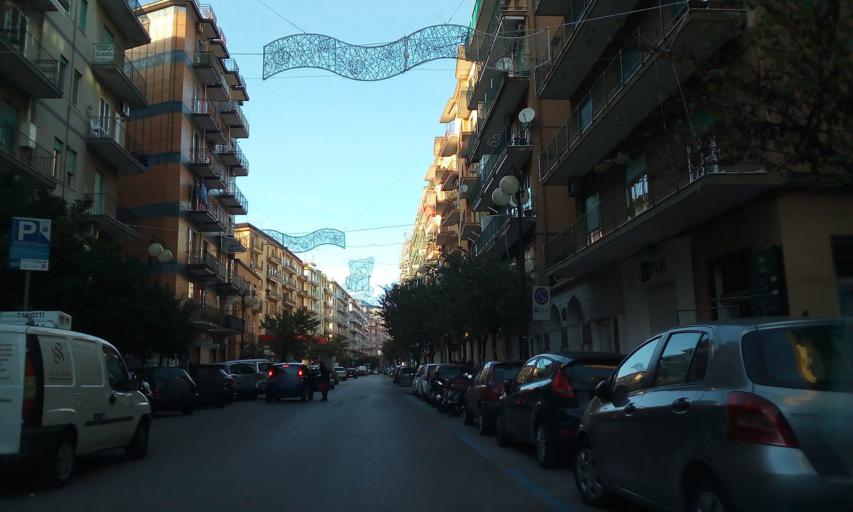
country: IT
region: Campania
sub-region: Provincia di Salerno
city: Salerno
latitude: 40.6763
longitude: 14.7771
